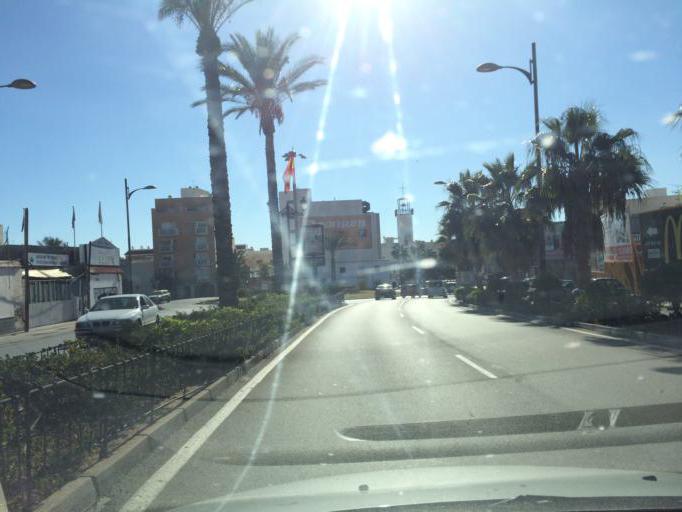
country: ES
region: Andalusia
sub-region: Provincia de Almeria
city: Aguadulce
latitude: 36.8098
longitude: -2.5976
